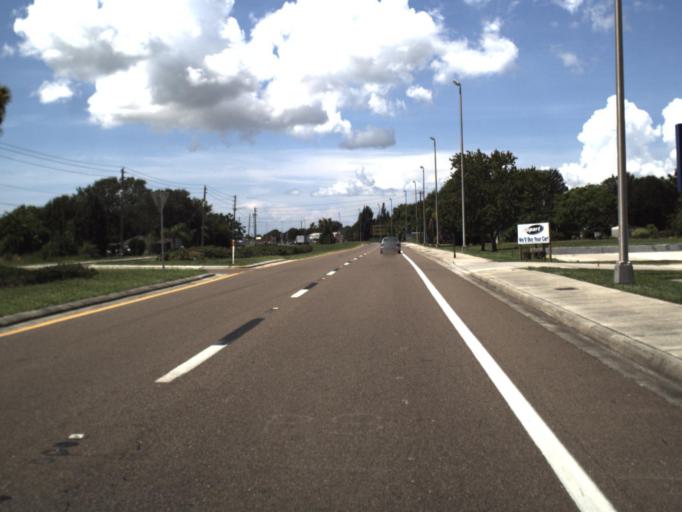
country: US
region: Florida
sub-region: Charlotte County
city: Cleveland
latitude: 26.9612
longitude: -81.9859
